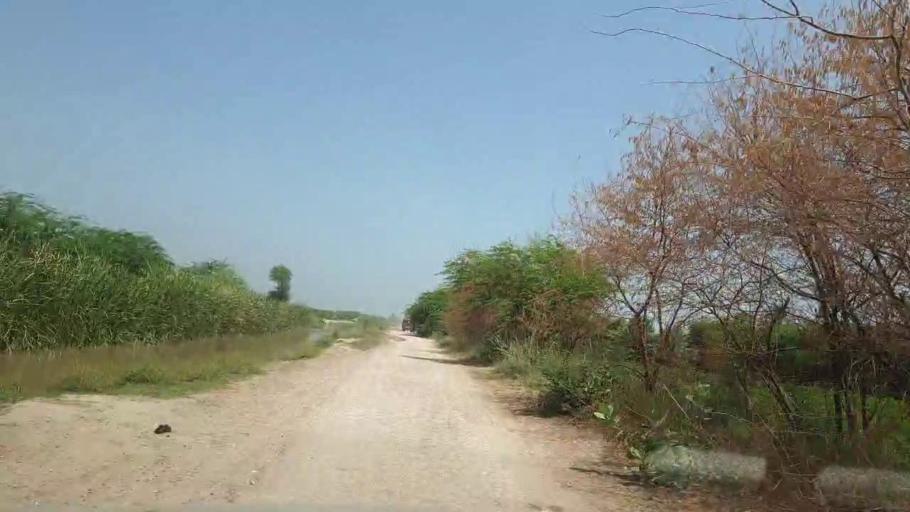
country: PK
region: Sindh
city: Rohri
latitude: 27.6332
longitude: 69.1002
